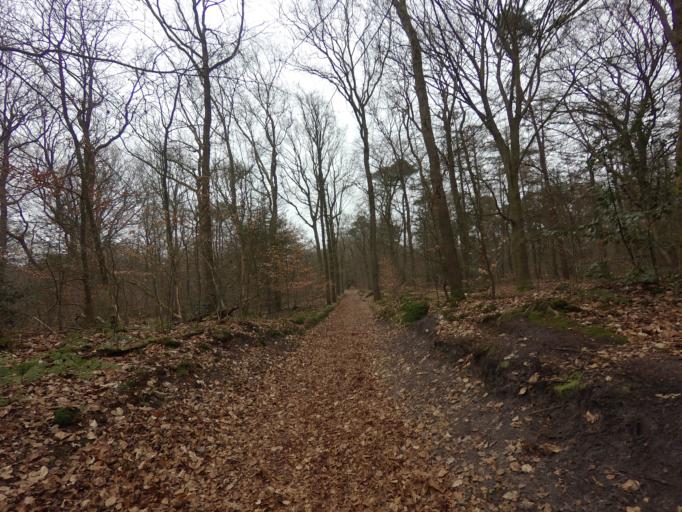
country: NL
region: Friesland
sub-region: Gemeente Gaasterlan-Sleat
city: Oudemirdum
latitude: 52.8558
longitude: 5.4866
